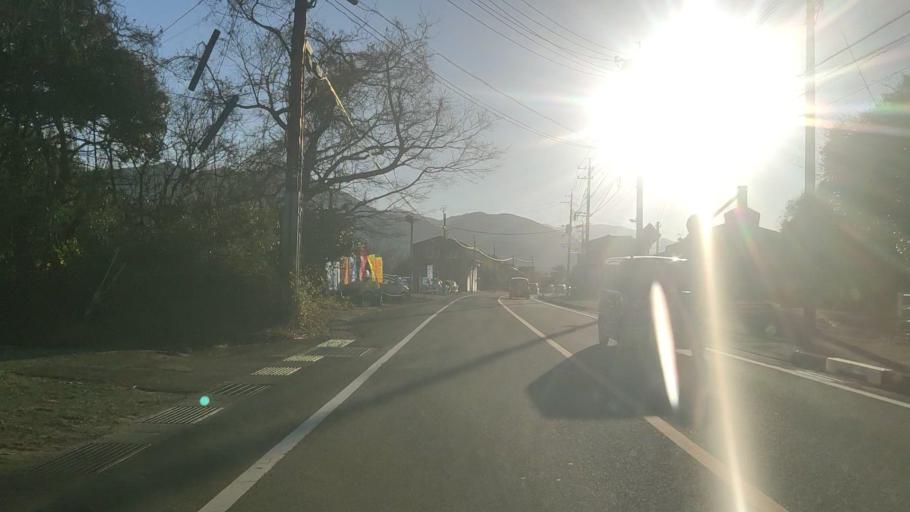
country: JP
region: Miyazaki
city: Miyazaki-shi
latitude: 31.8519
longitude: 131.3566
